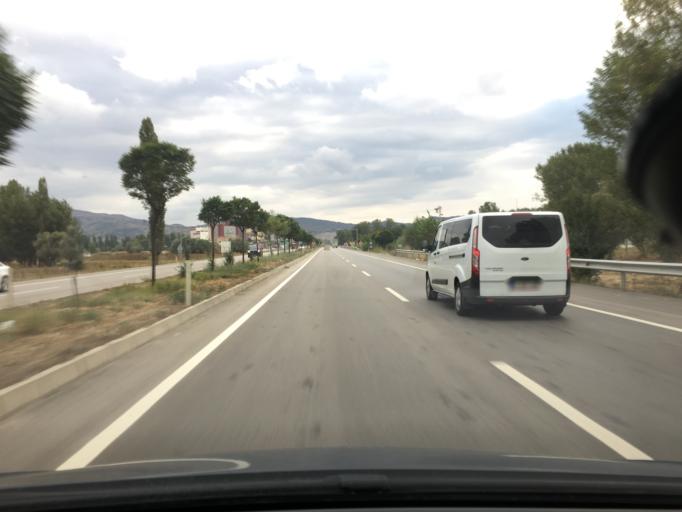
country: TR
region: Afyonkarahisar
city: Sincanli
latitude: 38.7497
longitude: 30.3574
